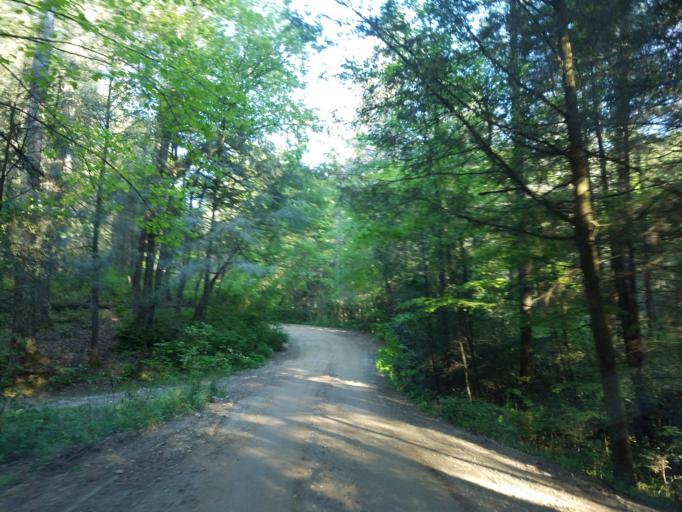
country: US
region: Georgia
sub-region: Lumpkin County
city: Dahlonega
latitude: 34.7002
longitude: -84.1454
